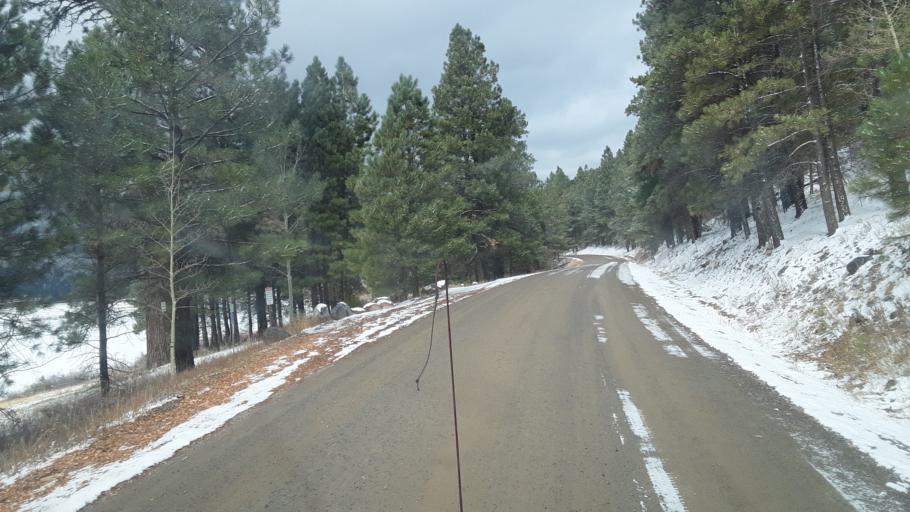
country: US
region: Colorado
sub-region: La Plata County
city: Bayfield
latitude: 37.4231
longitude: -107.5373
